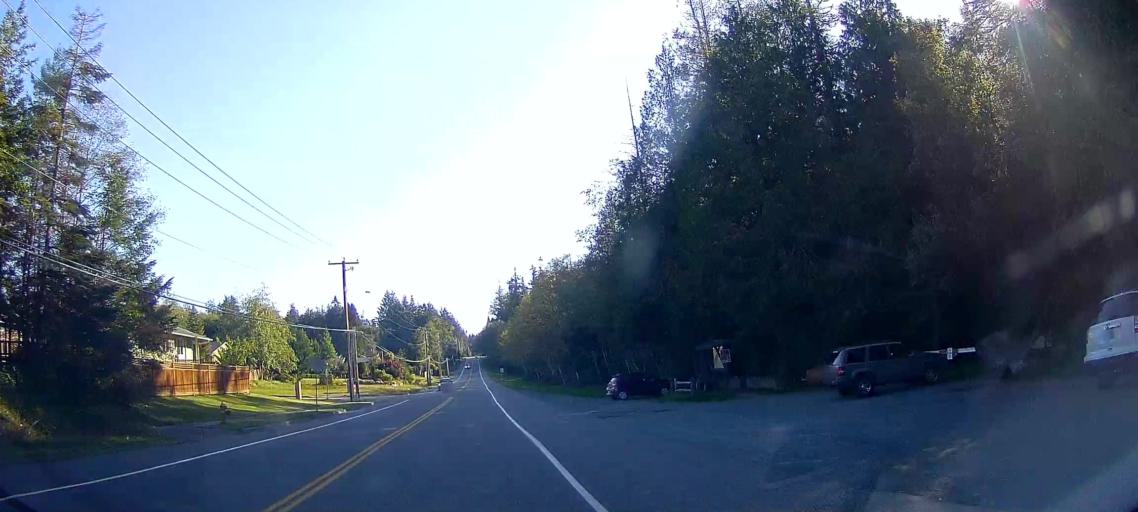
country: US
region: Washington
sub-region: Skagit County
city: Anacortes
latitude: 48.4916
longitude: -122.6364
